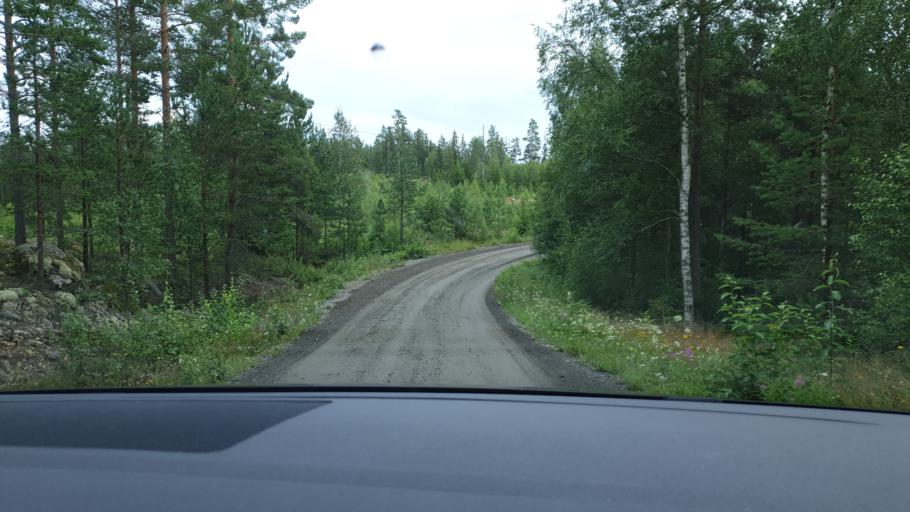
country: SE
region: Gaevleborg
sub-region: Hudiksvalls Kommun
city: Iggesund
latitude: 61.5281
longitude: 17.0123
